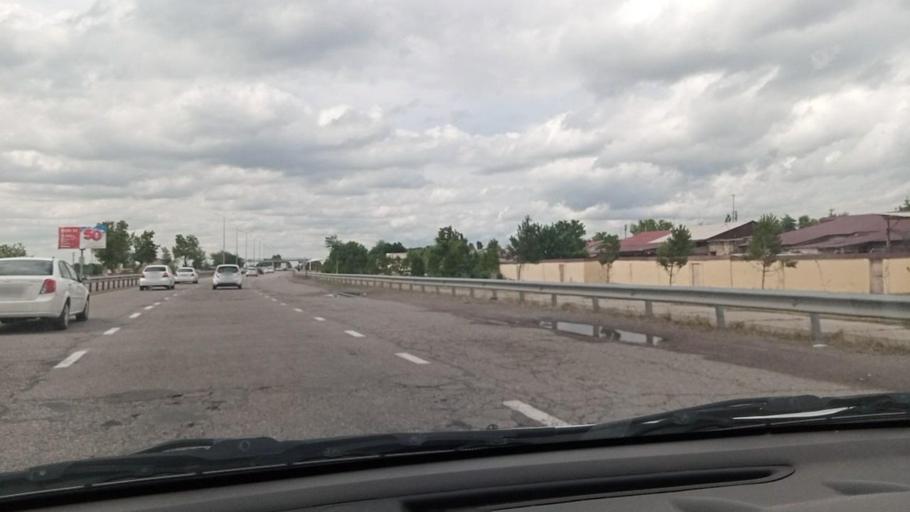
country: UZ
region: Toshkent
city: Tuytepa
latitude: 41.1264
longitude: 69.4379
